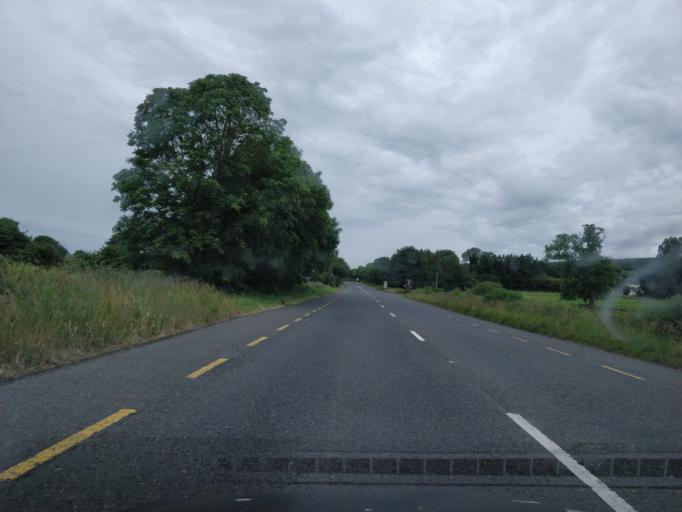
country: IE
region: Munster
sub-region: North Tipperary
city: Roscrea
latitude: 52.9572
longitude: -7.7071
